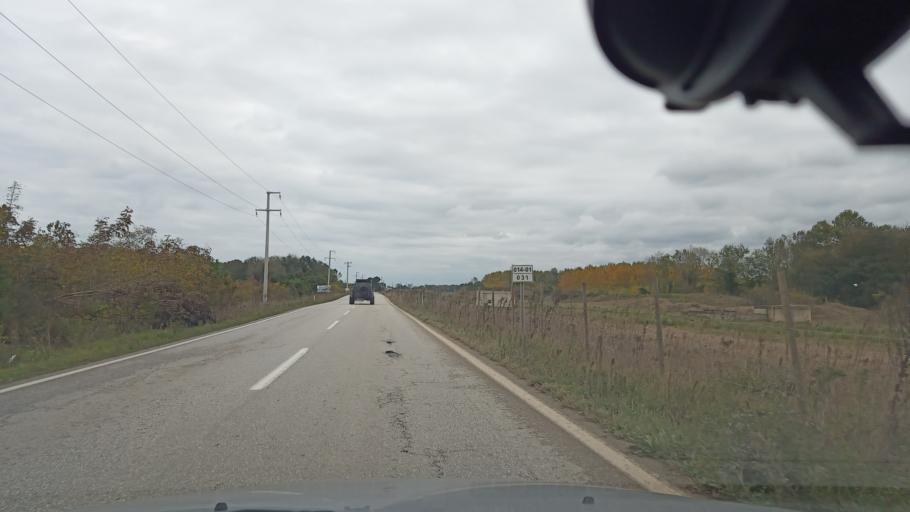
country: TR
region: Sakarya
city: Karasu
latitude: 41.1207
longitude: 30.5928
